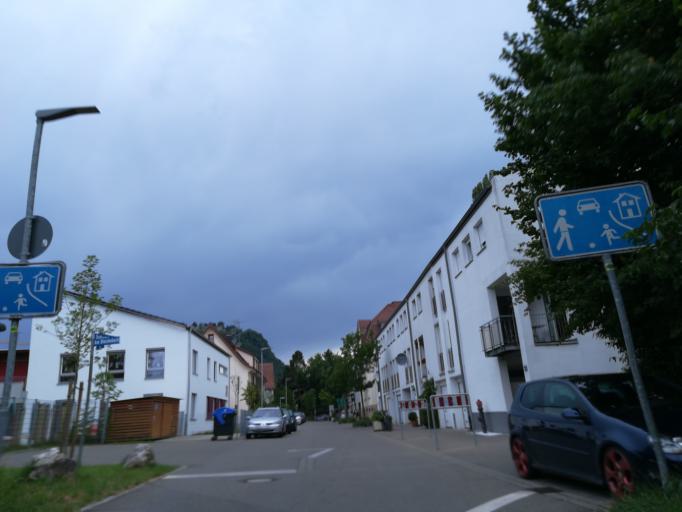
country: DE
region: Baden-Wuerttemberg
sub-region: Freiburg Region
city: Singen
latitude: 47.7561
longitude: 8.8342
